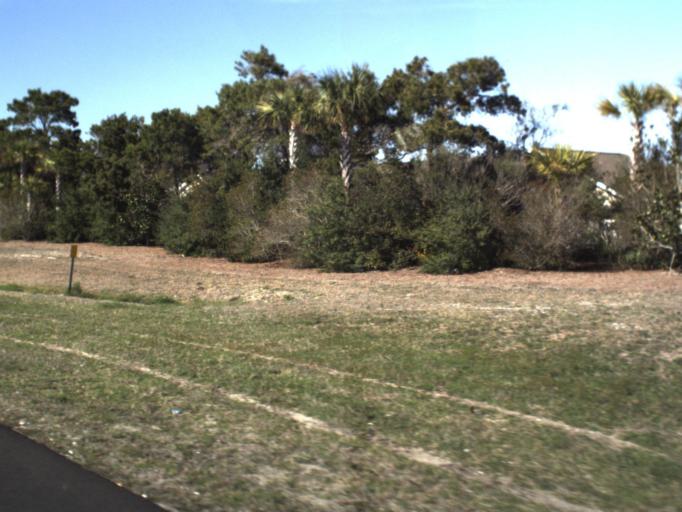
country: US
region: Florida
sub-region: Bay County
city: Laguna Beach
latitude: 30.2185
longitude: -85.8620
